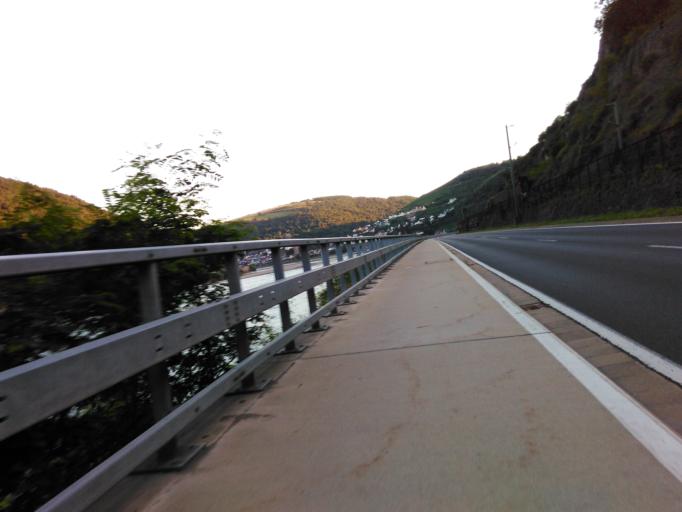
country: DE
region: Rheinland-Pfalz
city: Urbar
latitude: 50.1234
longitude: 7.7296
